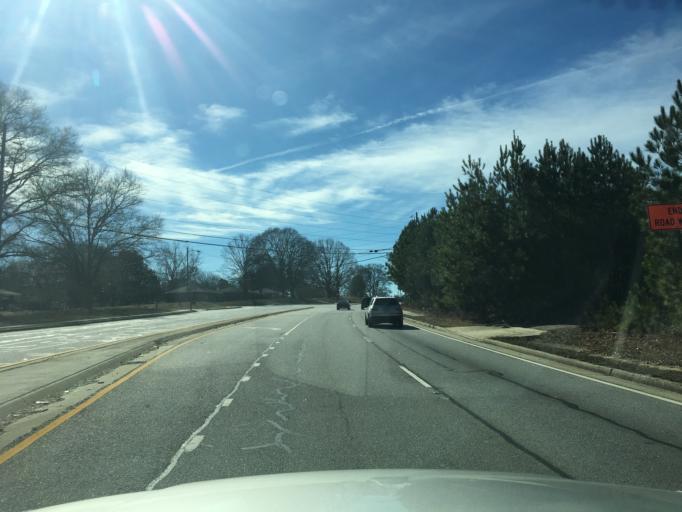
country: US
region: Georgia
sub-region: Gwinnett County
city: Snellville
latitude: 33.8496
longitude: -84.0240
